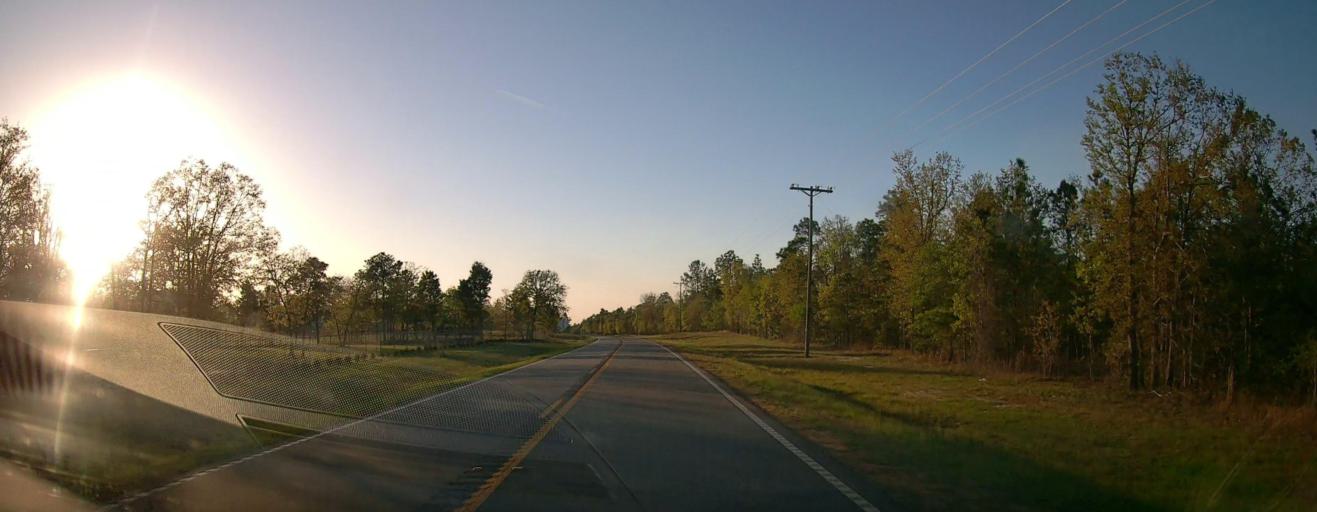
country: US
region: Georgia
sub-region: Talbot County
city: Talbotton
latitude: 32.5248
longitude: -84.4755
